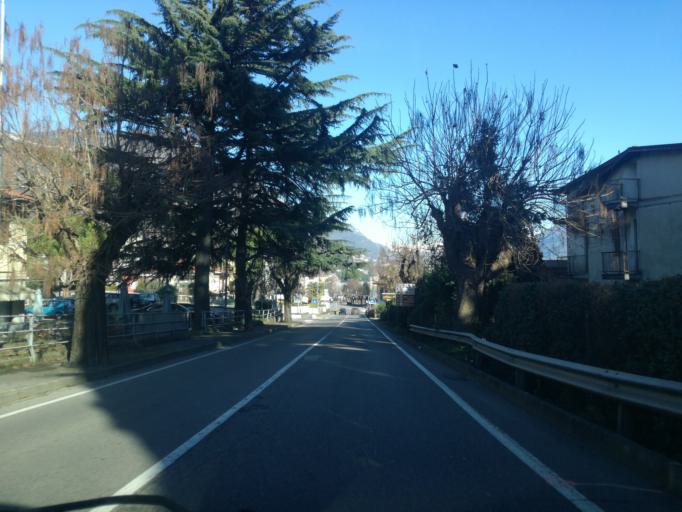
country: IT
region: Lombardy
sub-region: Provincia di Bergamo
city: Lovere
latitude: 45.8107
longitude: 10.0697
